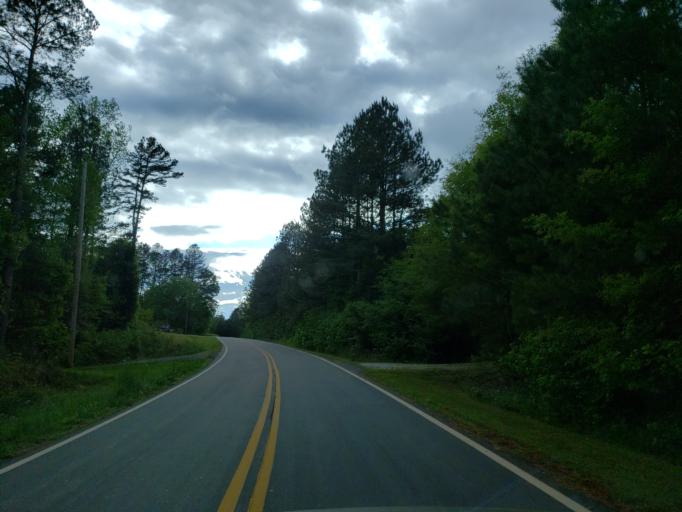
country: US
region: Georgia
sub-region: Haralson County
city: Tallapoosa
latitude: 33.8654
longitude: -85.3559
